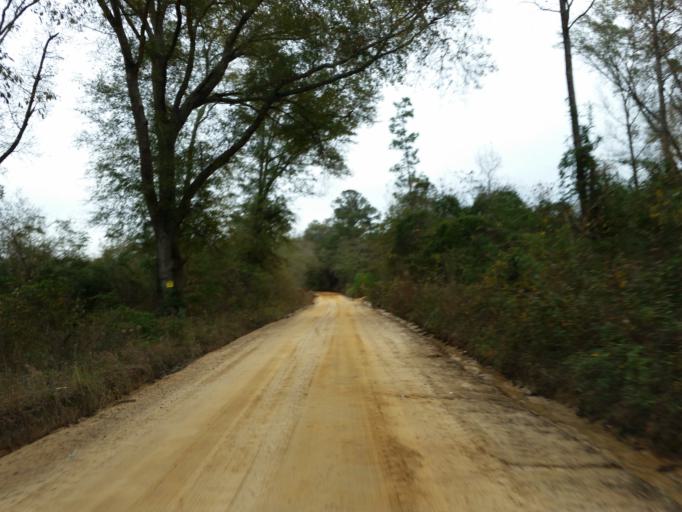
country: US
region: Georgia
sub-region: Crisp County
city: Cordele
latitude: 31.9078
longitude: -83.7320
